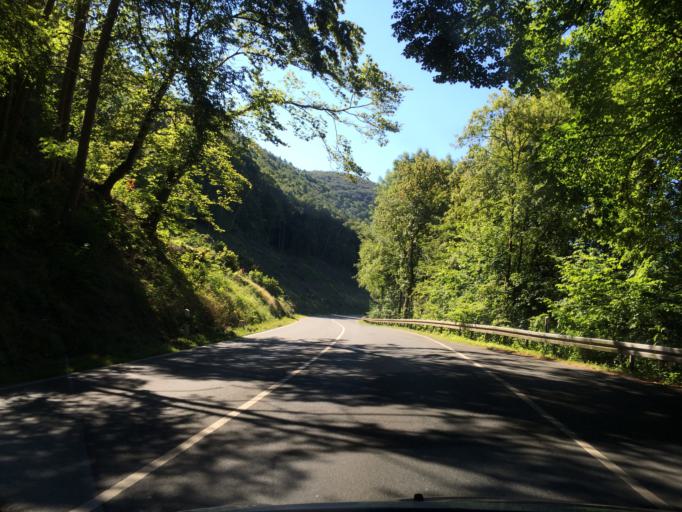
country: DE
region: North Rhine-Westphalia
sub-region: Regierungsbezirk Arnsberg
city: Nachrodt-Wiblingwerde
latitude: 51.3570
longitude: 7.6404
